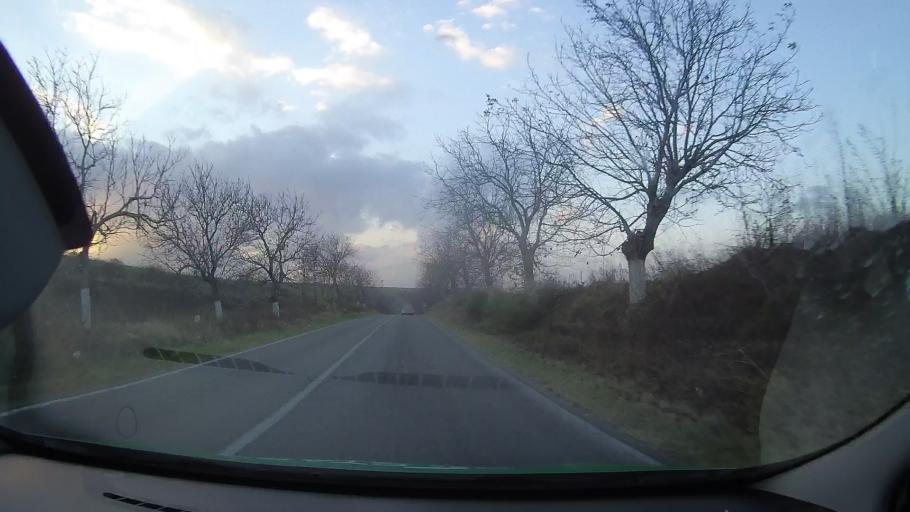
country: RO
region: Constanta
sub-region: Comuna Lipnita
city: Lipnita
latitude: 44.0950
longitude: 27.6391
